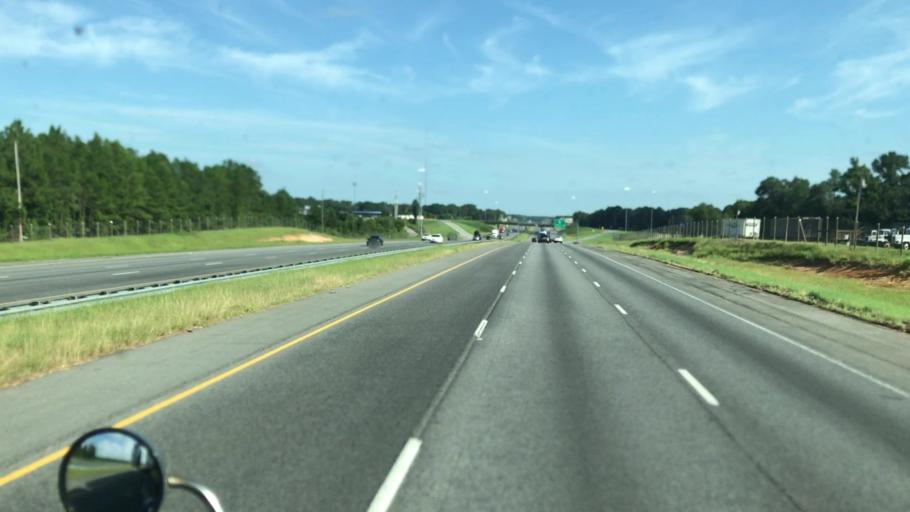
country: US
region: Georgia
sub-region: Crisp County
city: Cordele
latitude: 31.9014
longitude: -83.7357
